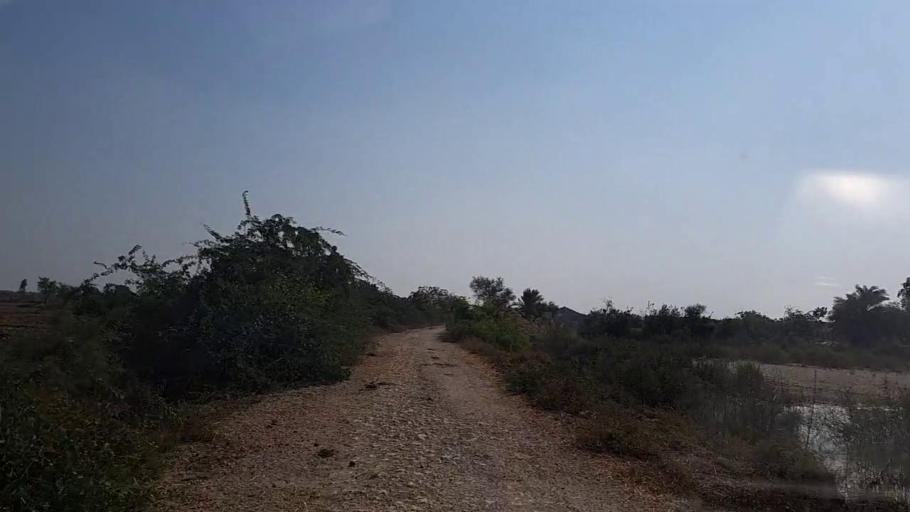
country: PK
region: Sindh
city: Thatta
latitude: 24.7946
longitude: 67.9691
